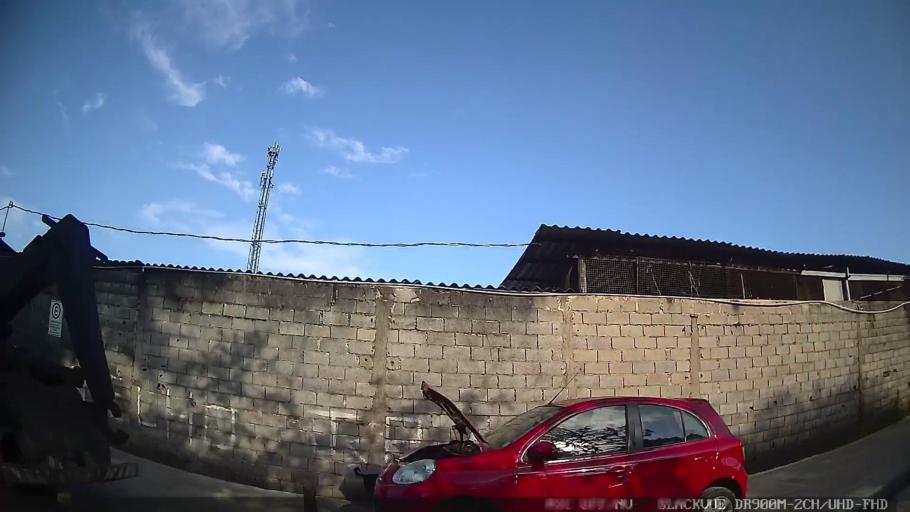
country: BR
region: Sao Paulo
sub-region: Itanhaem
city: Itanhaem
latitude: -24.1780
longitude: -46.8251
